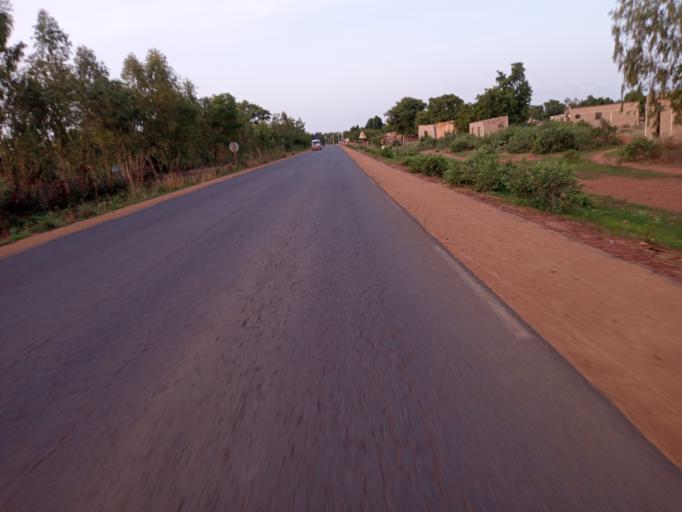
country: ML
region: Bamako
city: Bamako
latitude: 12.2975
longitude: -8.1619
